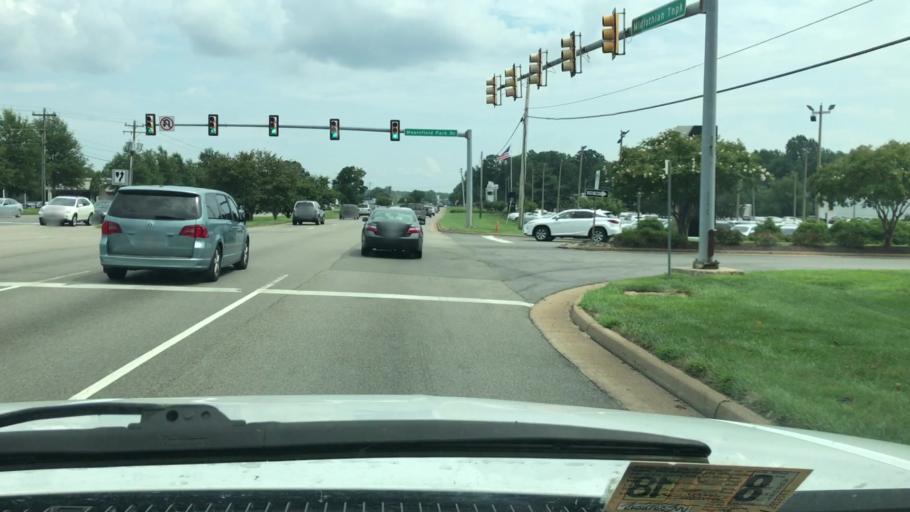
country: US
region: Virginia
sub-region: Chesterfield County
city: Bon Air
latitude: 37.5038
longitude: -77.5767
